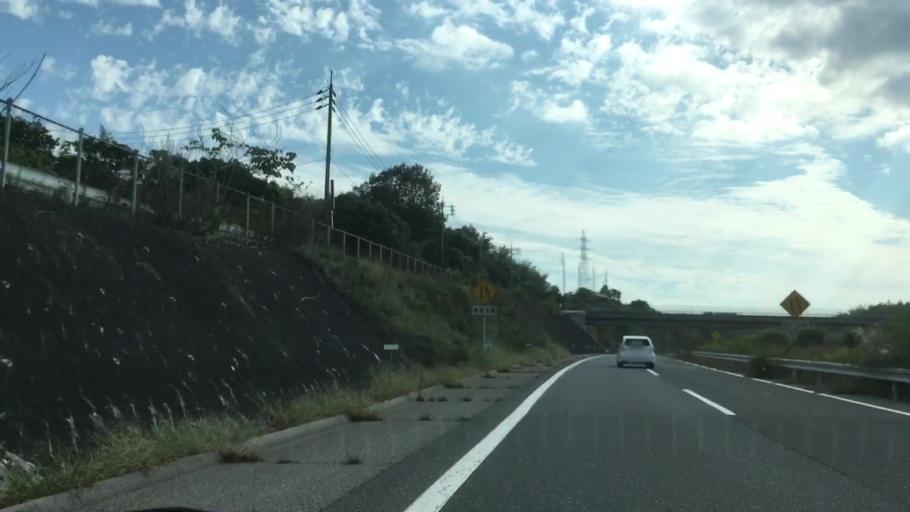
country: JP
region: Hiroshima
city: Hatsukaichi
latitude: 34.3326
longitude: 132.2946
